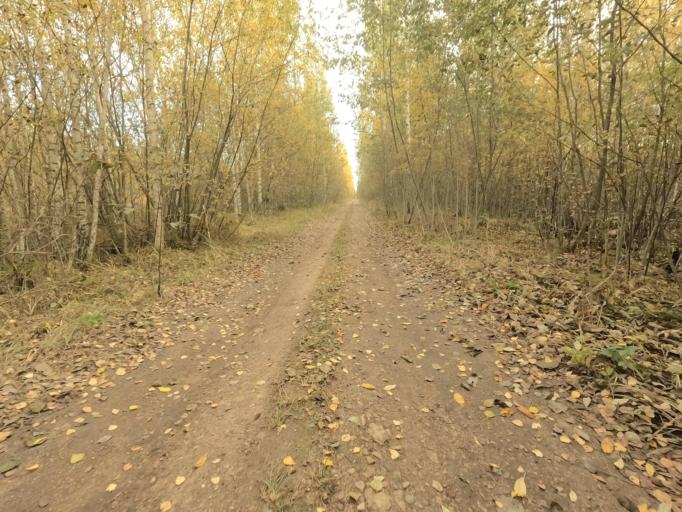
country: RU
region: Novgorod
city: Pankovka
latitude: 58.8789
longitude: 30.8555
